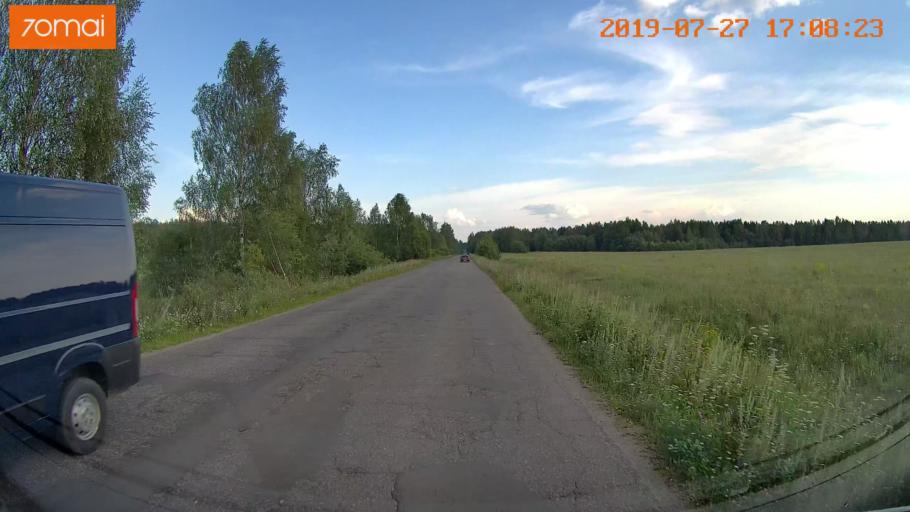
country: RU
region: Ivanovo
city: Novo-Talitsy
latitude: 57.0829
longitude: 40.8372
